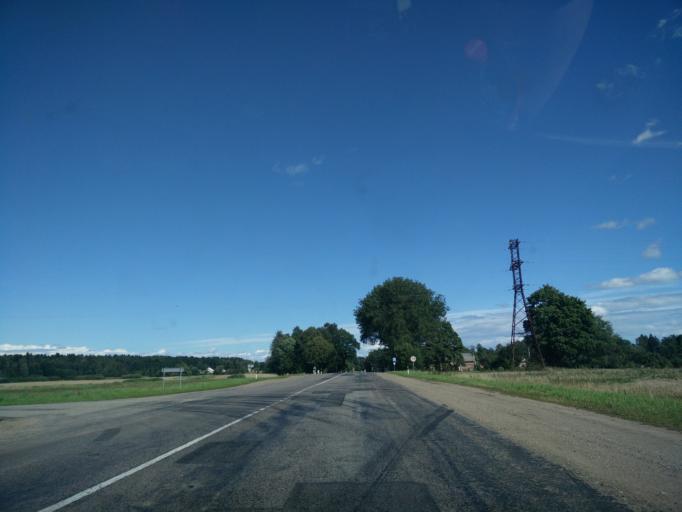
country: LT
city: Vilkija
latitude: 54.9810
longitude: 23.4682
